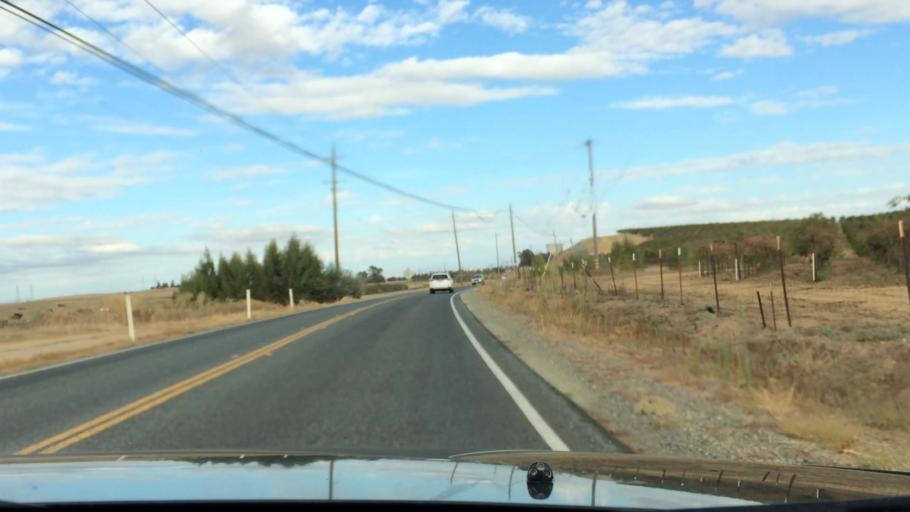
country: US
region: California
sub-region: Sacramento County
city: Clay
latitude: 38.3329
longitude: -121.1772
